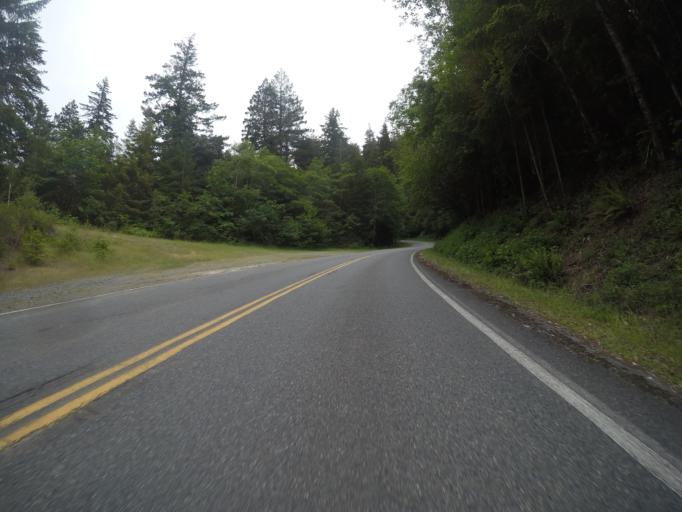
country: US
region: California
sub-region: Del Norte County
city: Bertsch-Oceanview
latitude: 41.7709
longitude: -124.0124
